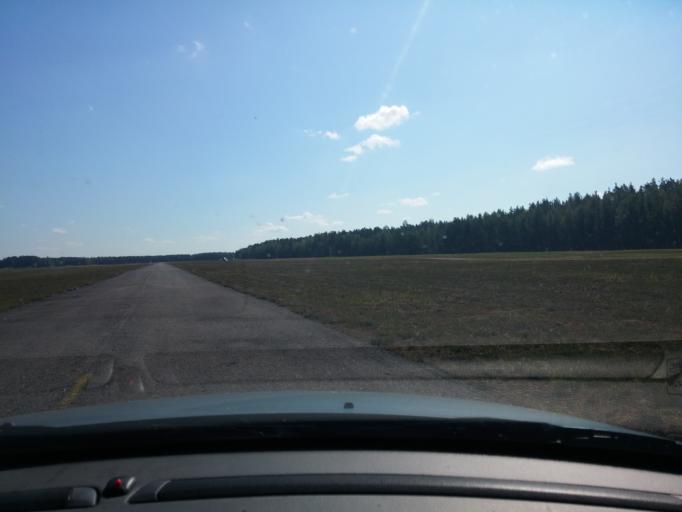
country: FI
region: Uusimaa
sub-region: Helsinki
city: Kaerkoelae
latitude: 60.7410
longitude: 24.0924
